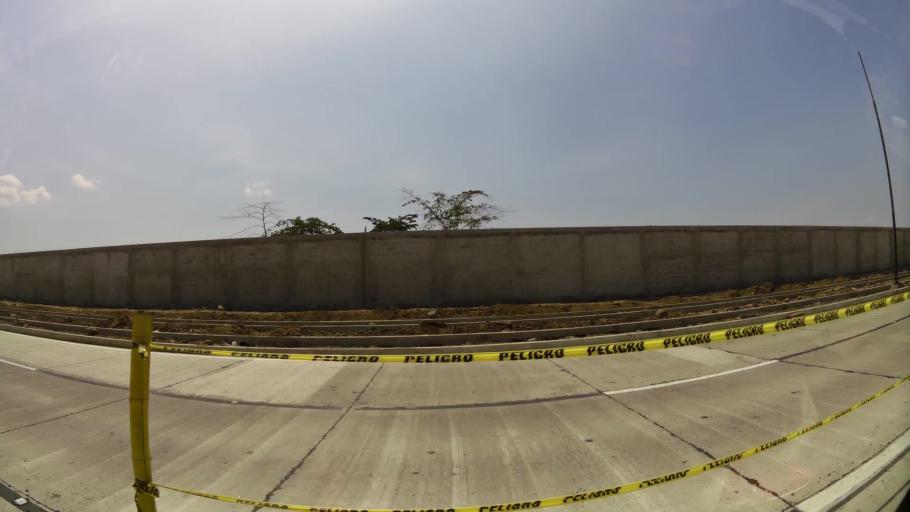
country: EC
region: Guayas
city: Eloy Alfaro
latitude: -2.0739
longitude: -79.8677
